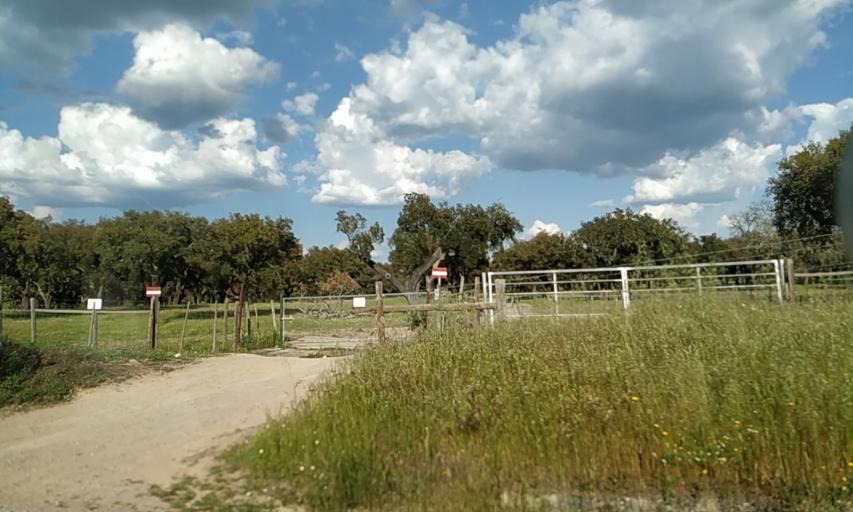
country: PT
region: Portalegre
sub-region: Portalegre
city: Urra
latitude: 39.2278
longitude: -7.4552
